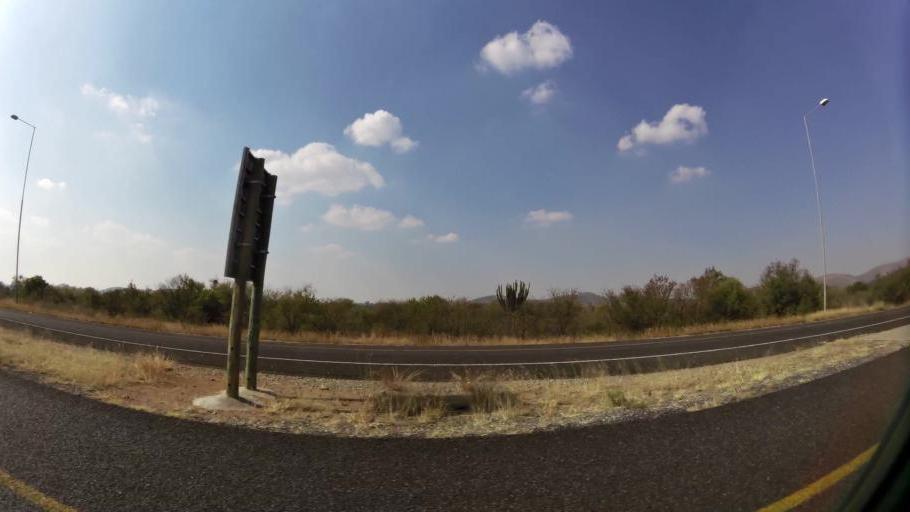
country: ZA
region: North-West
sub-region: Bojanala Platinum District Municipality
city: Rustenburg
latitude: -25.6160
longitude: 27.1543
